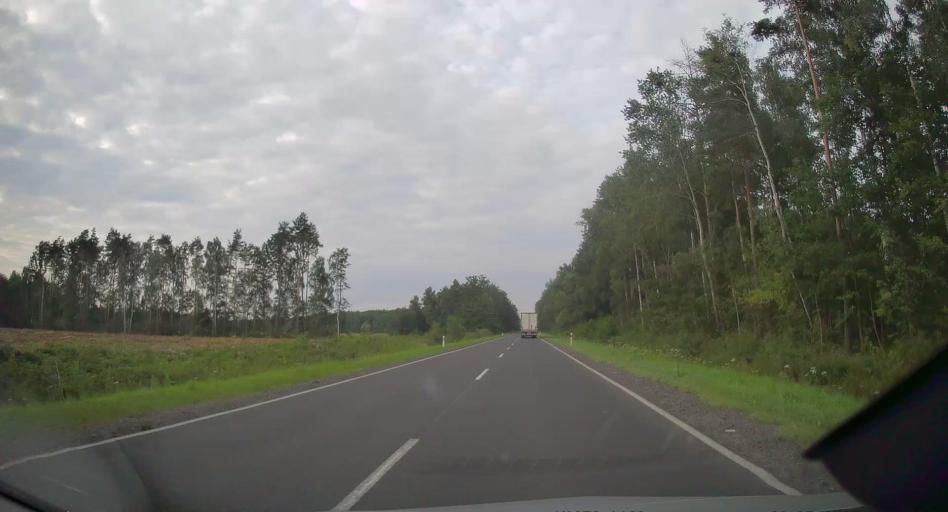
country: PL
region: Lodz Voivodeship
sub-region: Powiat radomszczanski
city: Plawno
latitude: 50.9767
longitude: 19.4098
